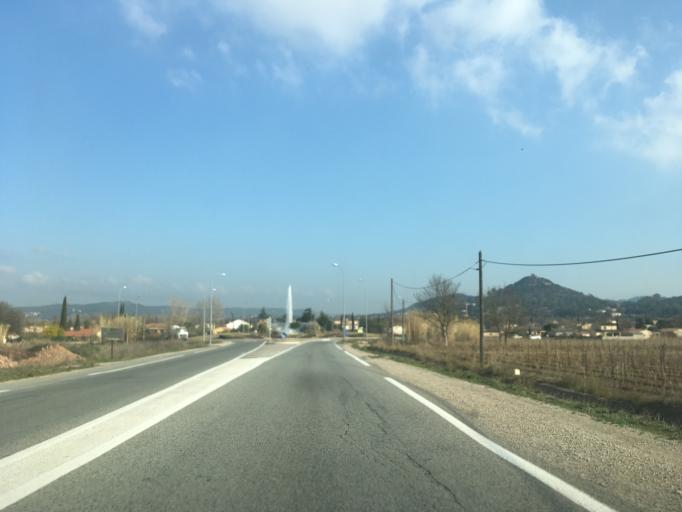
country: FR
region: Provence-Alpes-Cote d'Azur
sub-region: Departement du Var
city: Vidauban
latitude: 43.4132
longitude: 6.4177
